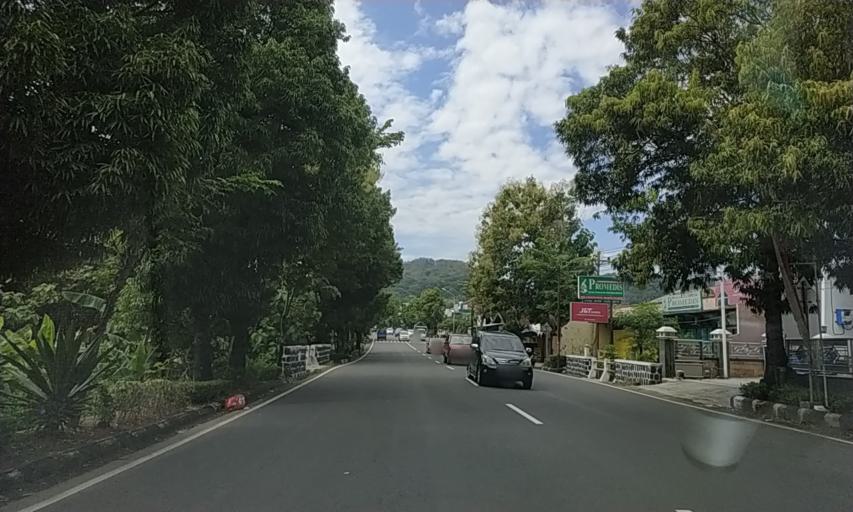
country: ID
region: Central Java
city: Selogiri
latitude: -7.8026
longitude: 110.9126
